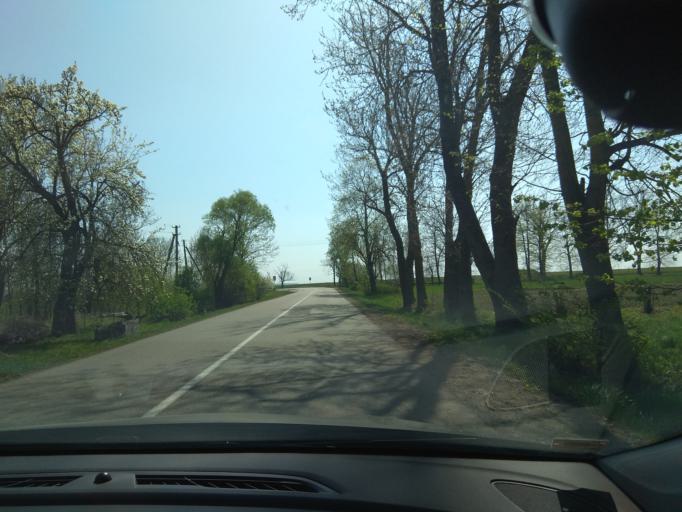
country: LT
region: Panevezys
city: Pasvalys
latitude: 55.9645
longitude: 24.2080
